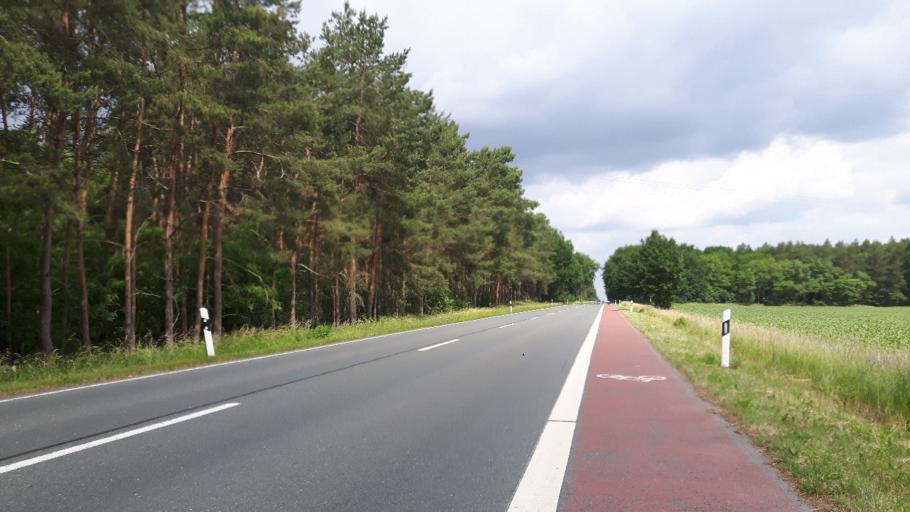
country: DE
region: Saxony-Anhalt
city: Schlaitz
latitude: 51.6742
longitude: 12.4447
